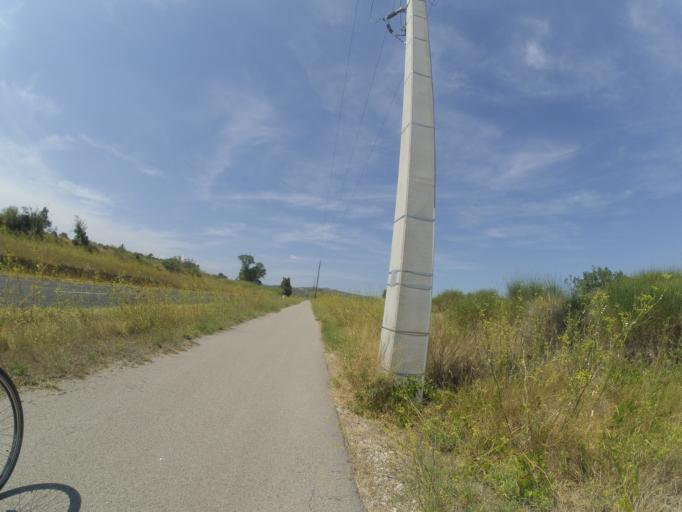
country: FR
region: Languedoc-Roussillon
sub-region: Departement des Pyrenees-Orientales
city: Peyrestortes
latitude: 42.7561
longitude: 2.8393
